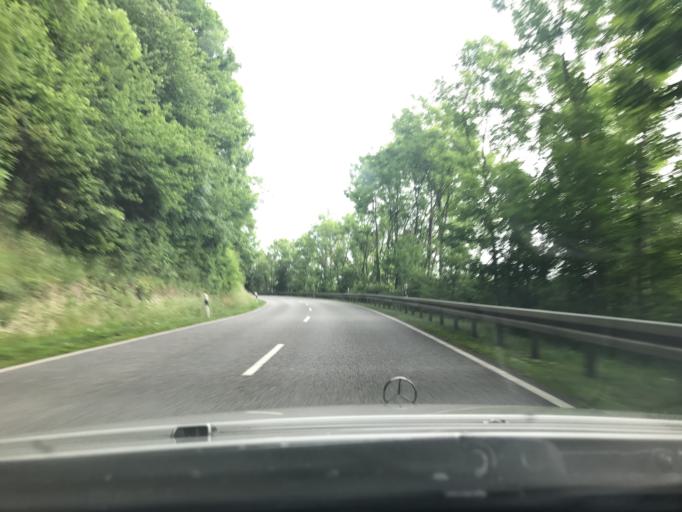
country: DE
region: Thuringia
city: Geisleden
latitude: 51.3544
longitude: 10.1863
